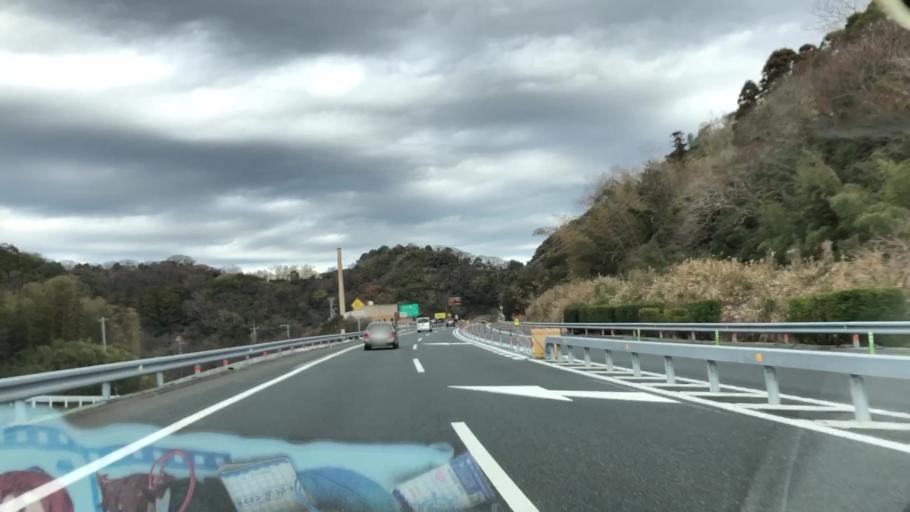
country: JP
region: Chiba
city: Tateyama
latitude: 35.1028
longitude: 139.8543
